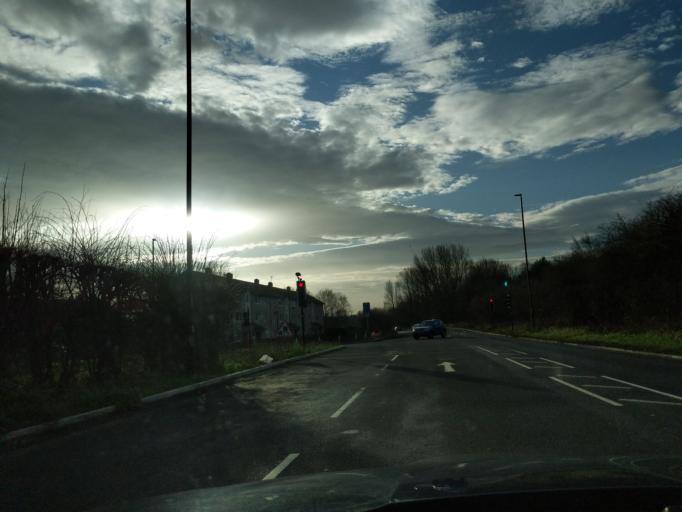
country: GB
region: England
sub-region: Newcastle upon Tyne
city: Gosforth
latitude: 55.0133
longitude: -1.6005
